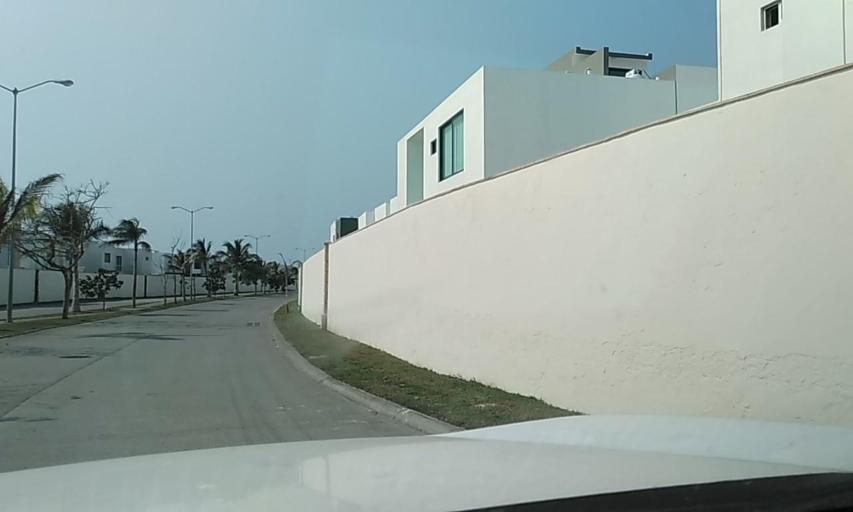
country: MX
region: Veracruz
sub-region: Alvarado
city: Playa de la Libertad
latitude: 19.0488
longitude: -96.0613
